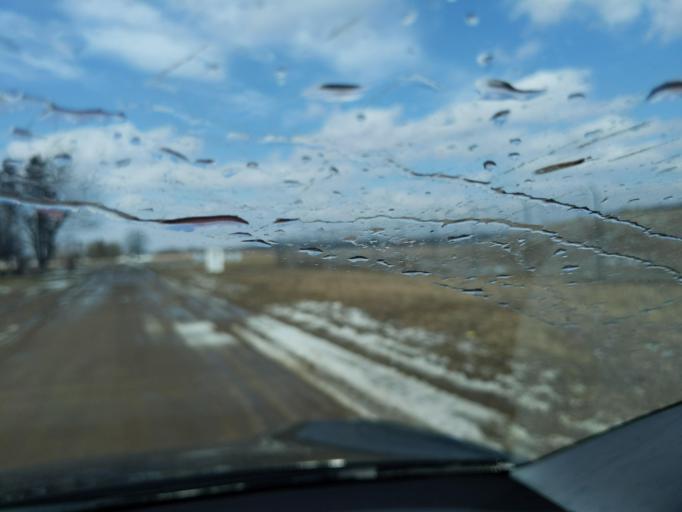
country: US
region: Michigan
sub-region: Livingston County
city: Fowlerville
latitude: 42.6243
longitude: -84.0619
